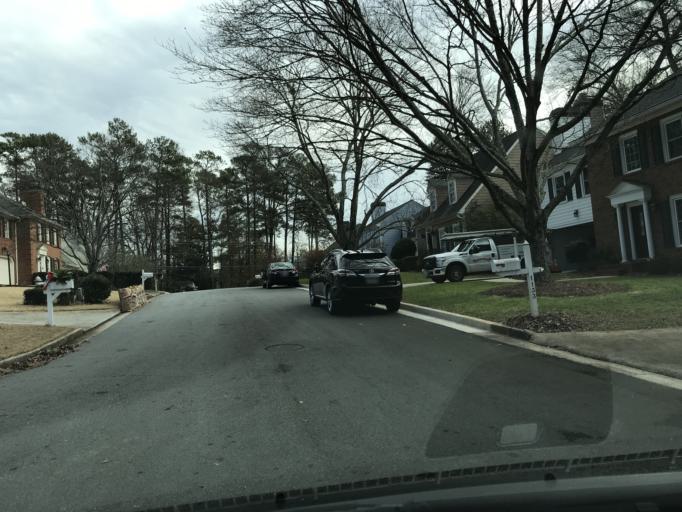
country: US
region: Georgia
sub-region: DeKalb County
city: North Atlanta
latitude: 33.8717
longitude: -84.3429
